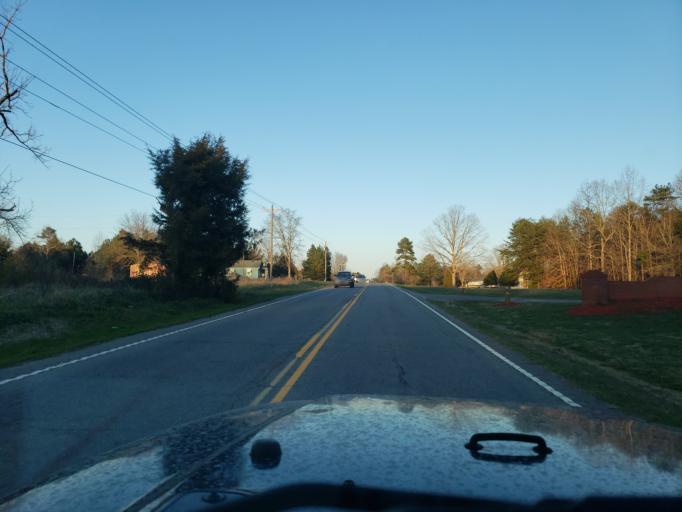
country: US
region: South Carolina
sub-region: York County
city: Clover
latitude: 35.1116
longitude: -81.3140
